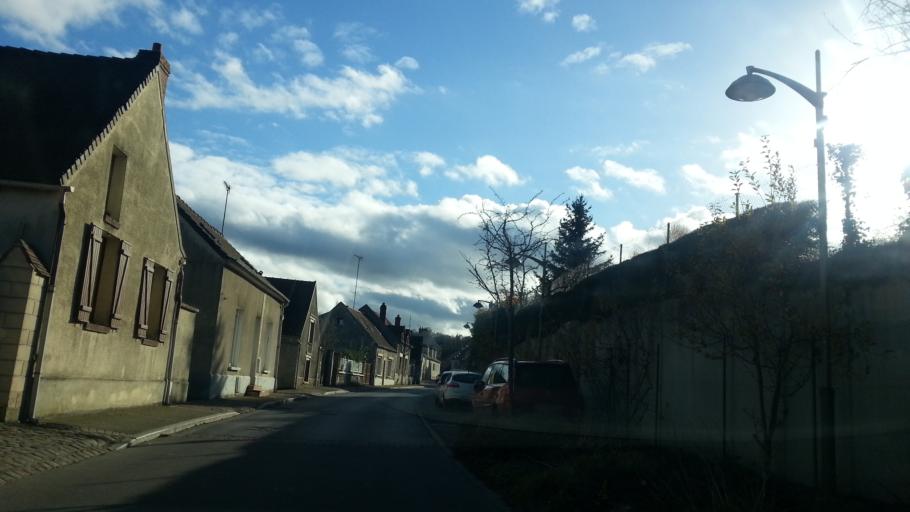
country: FR
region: Picardie
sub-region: Departement de l'Oise
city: Verneuil-en-Halatte
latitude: 49.2771
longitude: 2.5160
